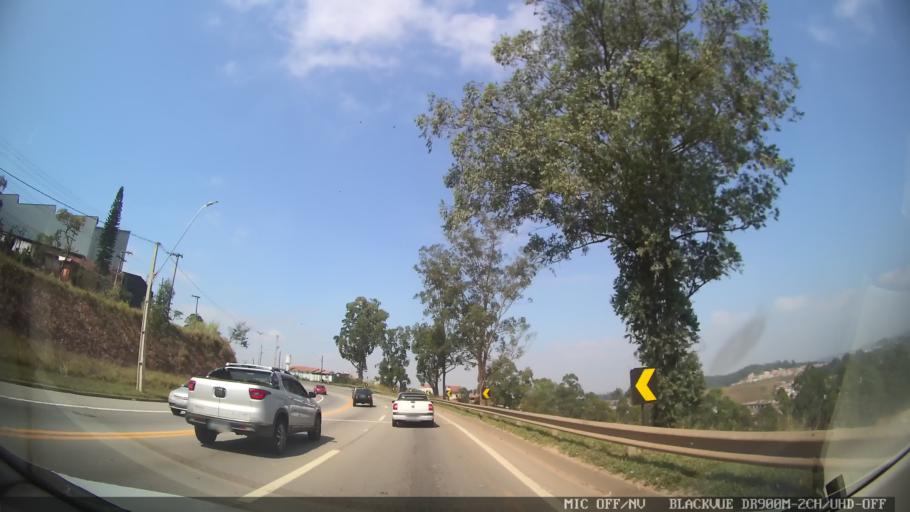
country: BR
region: Sao Paulo
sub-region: Caieiras
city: Caieiras
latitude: -23.3899
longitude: -46.7296
